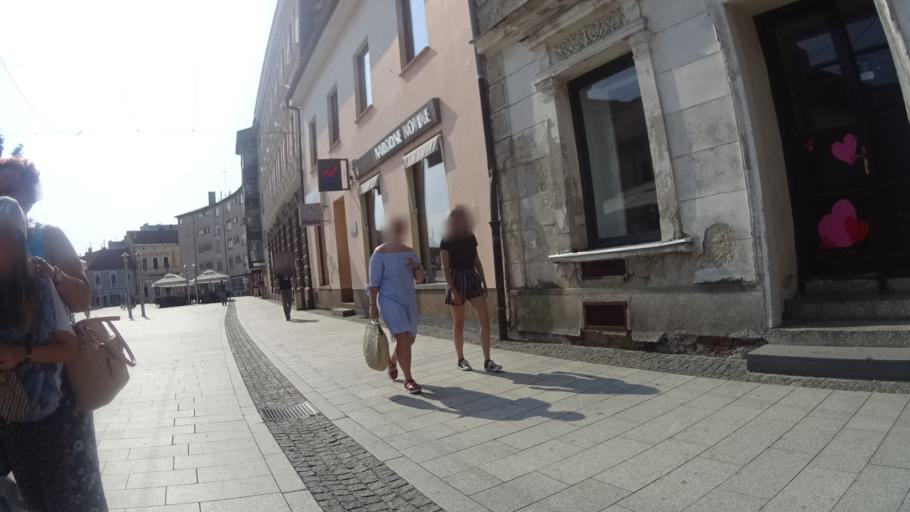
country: HR
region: Medimurska
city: Cakovec
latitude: 46.3900
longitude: 16.4371
